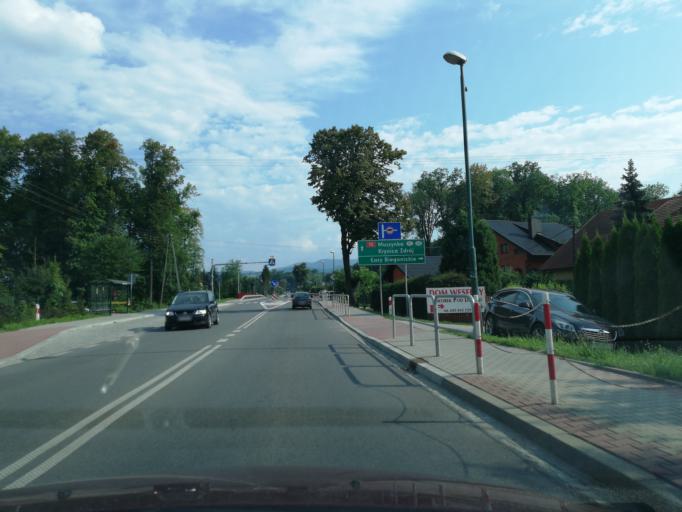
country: PL
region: Lesser Poland Voivodeship
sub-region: Powiat nowosadecki
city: Nawojowa
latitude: 49.5665
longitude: 20.7396
